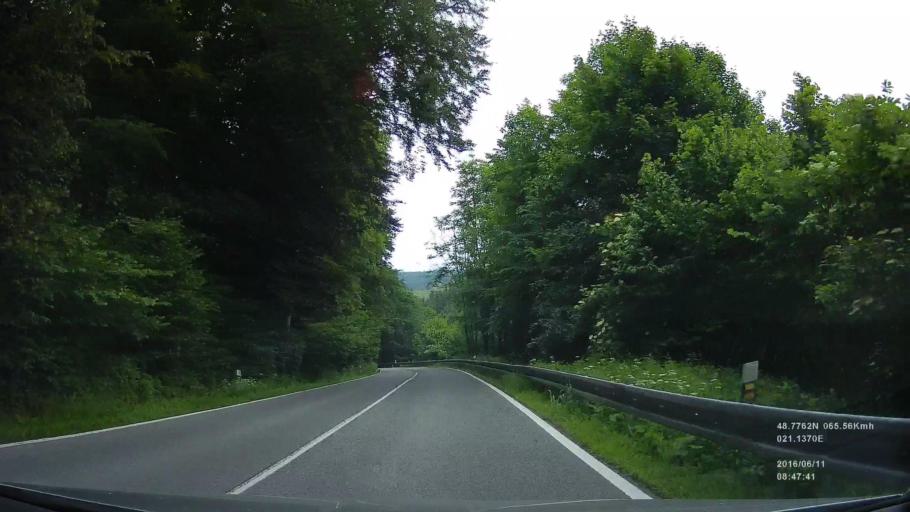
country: SK
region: Kosicky
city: Kosice
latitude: 48.7773
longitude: 21.1400
